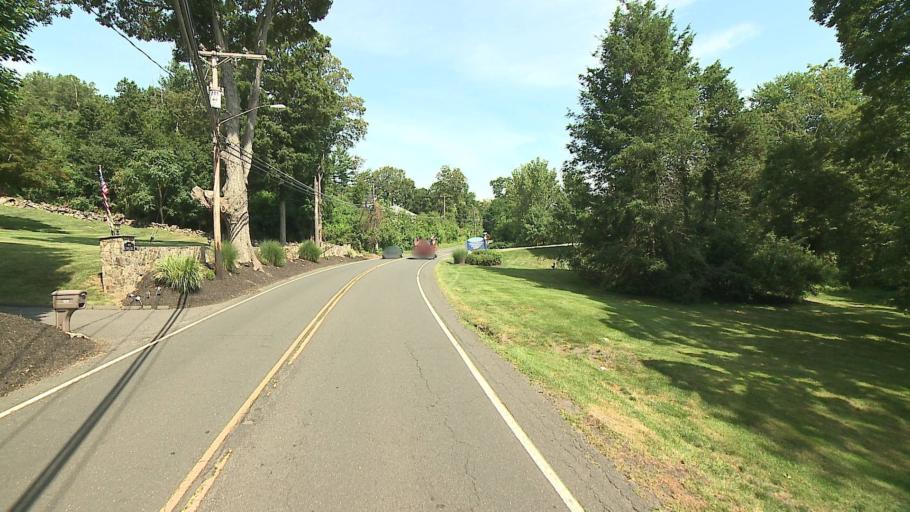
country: US
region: Connecticut
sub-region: Fairfield County
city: Danbury
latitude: 41.4235
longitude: -73.4821
